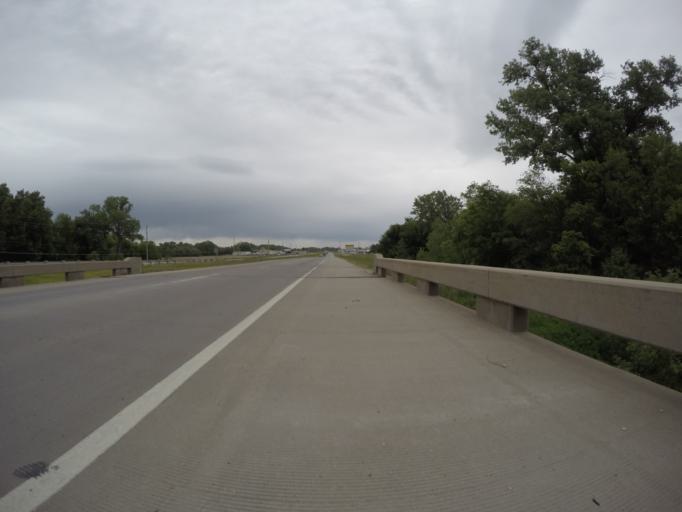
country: US
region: Kansas
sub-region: Riley County
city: Manhattan
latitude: 39.1924
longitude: -96.5371
